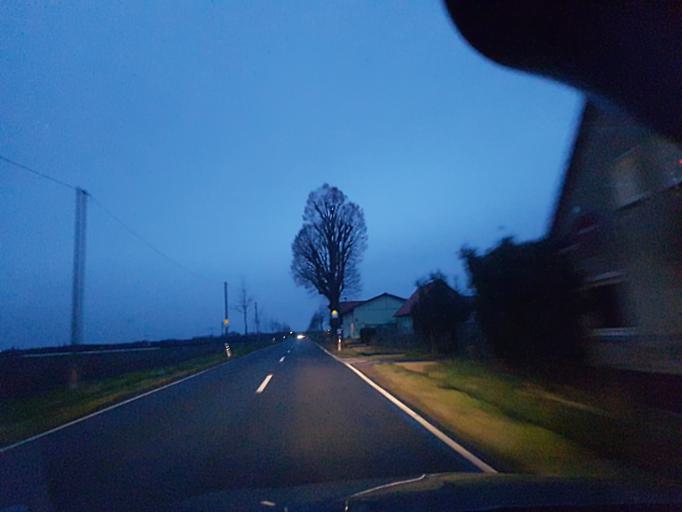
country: DE
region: Brandenburg
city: Doberlug-Kirchhain
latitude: 51.6164
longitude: 13.5797
